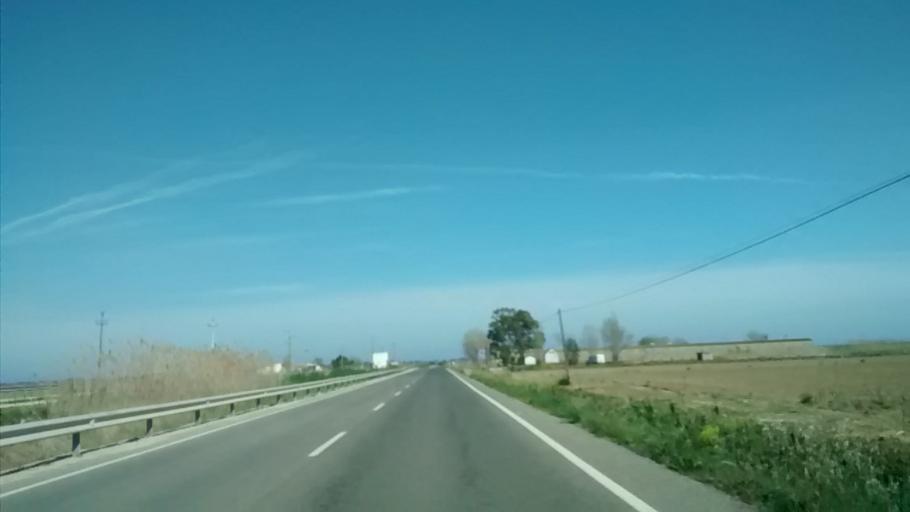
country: ES
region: Catalonia
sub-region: Provincia de Tarragona
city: Deltebre
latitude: 40.7051
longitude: 0.7835
